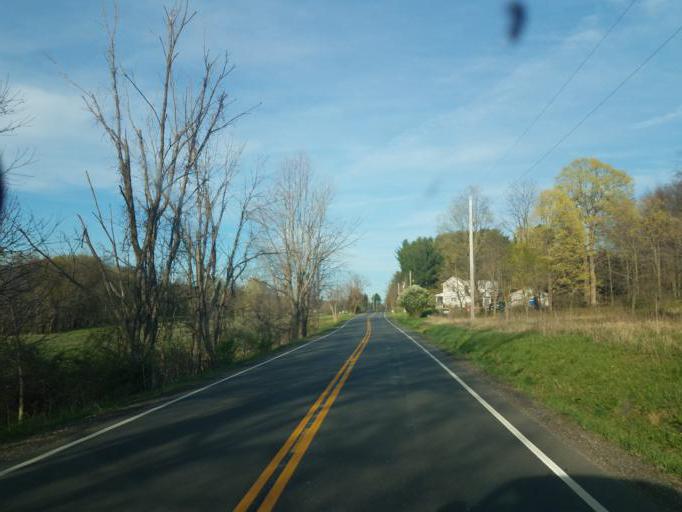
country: US
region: Ohio
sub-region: Crawford County
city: Crestline
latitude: 40.7028
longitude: -82.6810
